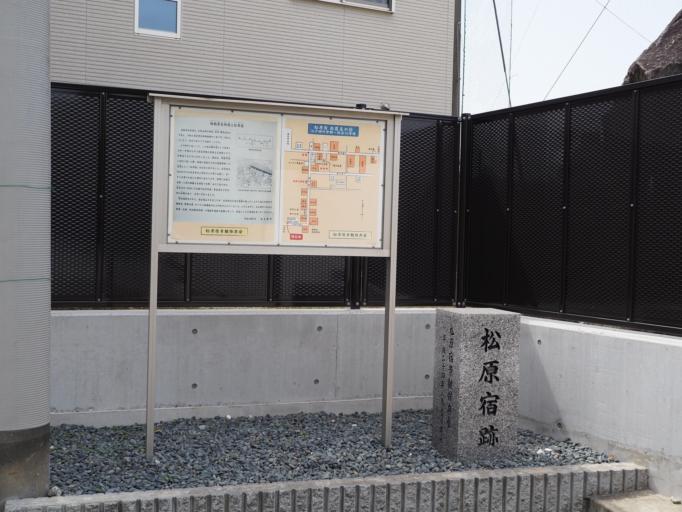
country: JP
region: Osaka
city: Daitocho
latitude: 34.6722
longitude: 135.6263
